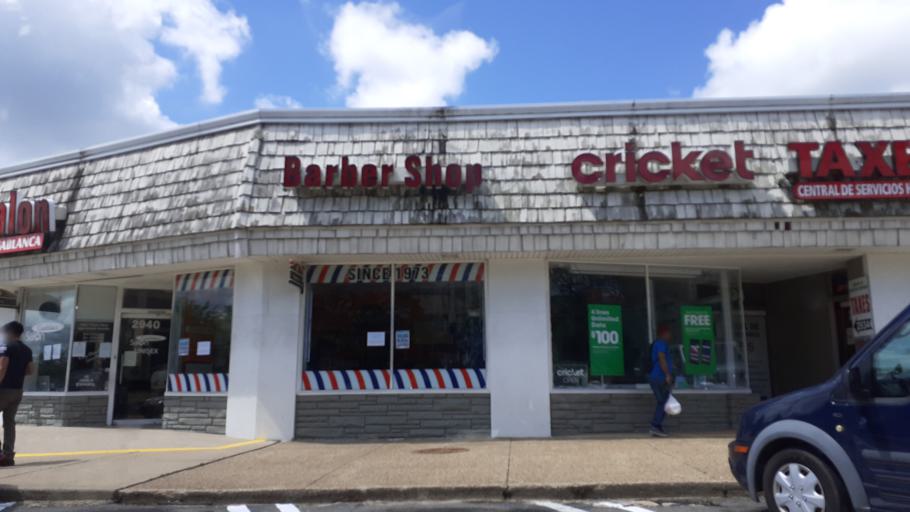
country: US
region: Virginia
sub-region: Fairfax County
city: Seven Corners
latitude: 38.8703
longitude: -77.1464
